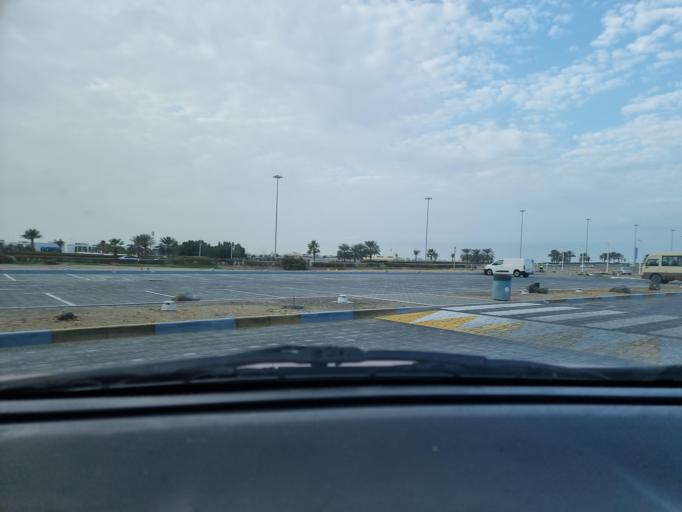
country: AE
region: Abu Dhabi
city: Abu Dhabi
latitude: 24.5019
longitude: 54.5887
